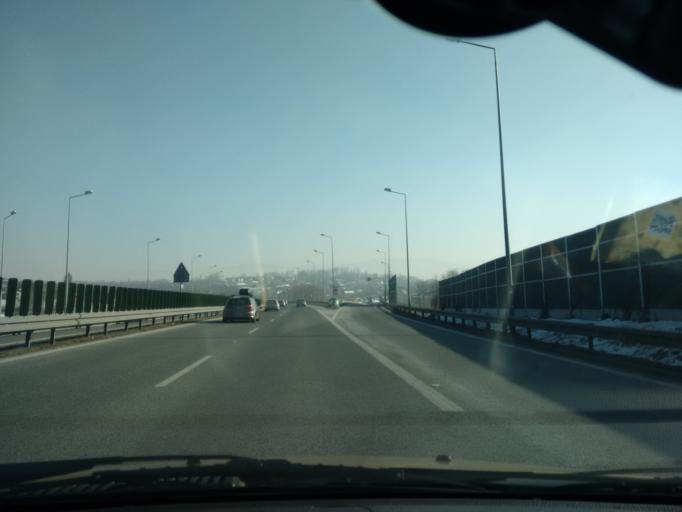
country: PL
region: Silesian Voivodeship
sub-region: Bielsko-Biala
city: Bielsko-Biala
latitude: 49.8458
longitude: 19.0657
